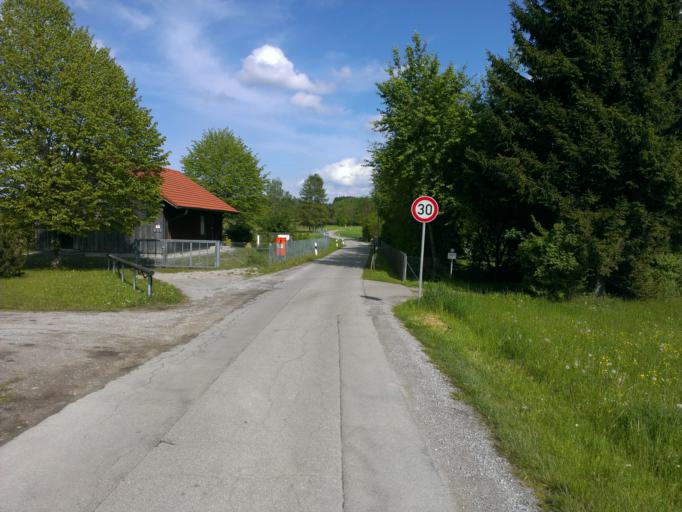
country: DE
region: Bavaria
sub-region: Upper Bavaria
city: Schaftlarn
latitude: 48.0113
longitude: 11.4080
